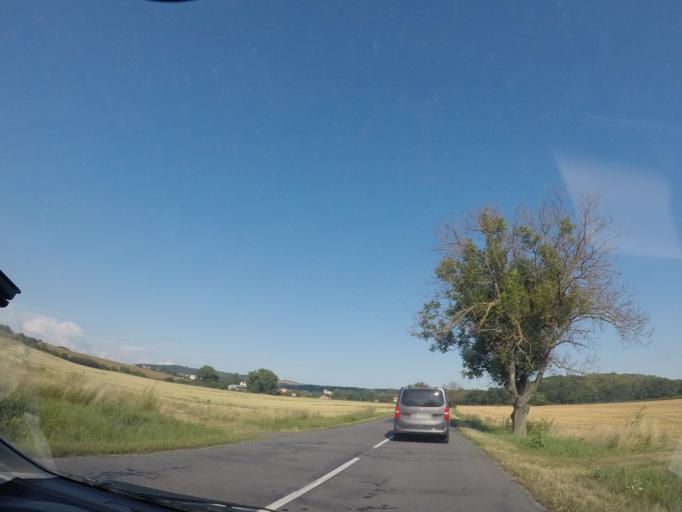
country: SK
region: Banskobystricky
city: Dudince
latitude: 48.1689
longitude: 18.8663
